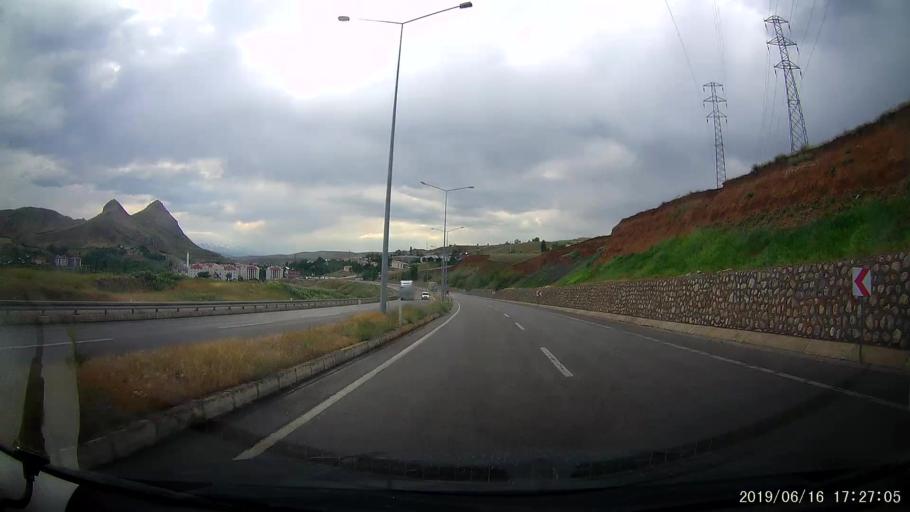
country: TR
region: Erzincan
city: Tercan
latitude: 39.7745
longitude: 40.3999
